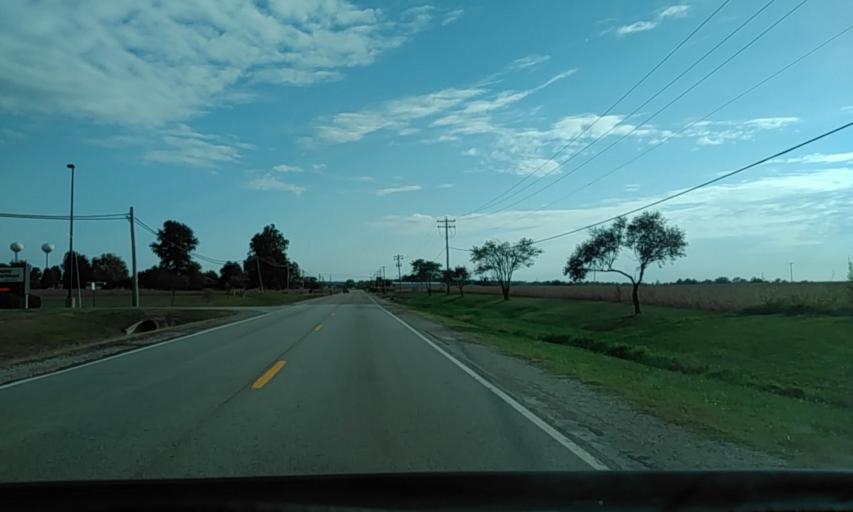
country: US
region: Illinois
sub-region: Bond County
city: Greenville
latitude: 38.8789
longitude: -89.4144
